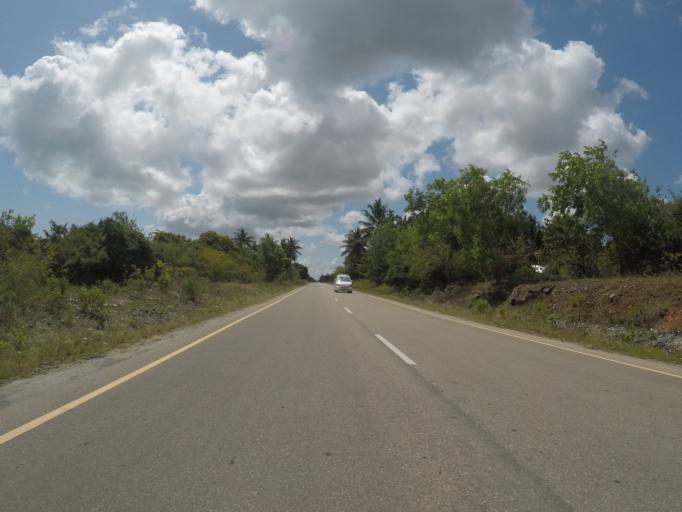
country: TZ
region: Zanzibar Central/South
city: Koani
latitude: -6.2694
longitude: 39.3623
